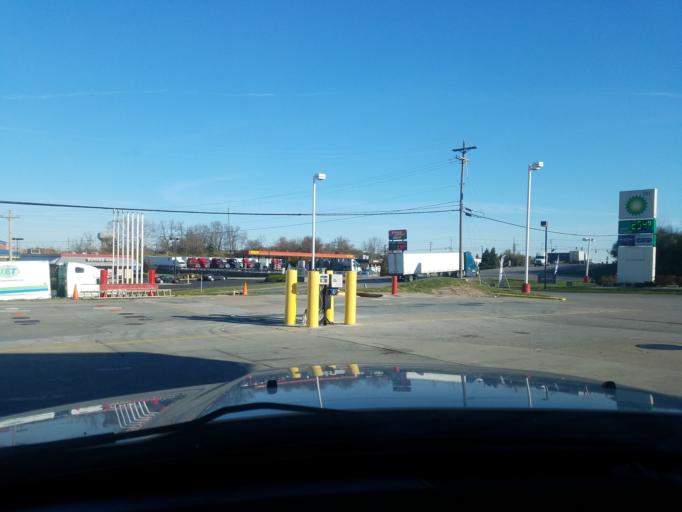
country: US
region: Kentucky
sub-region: Boone County
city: Walton
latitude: 38.9176
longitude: -84.6265
